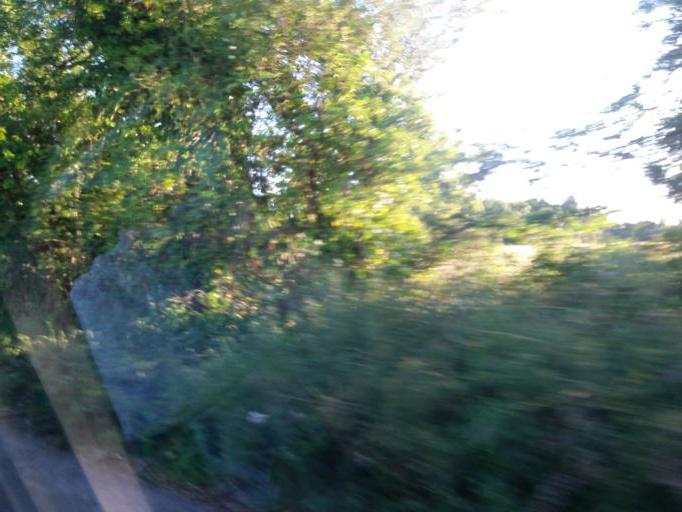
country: IE
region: Leinster
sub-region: An Mhi
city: Ashbourne
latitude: 53.5700
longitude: -6.3512
